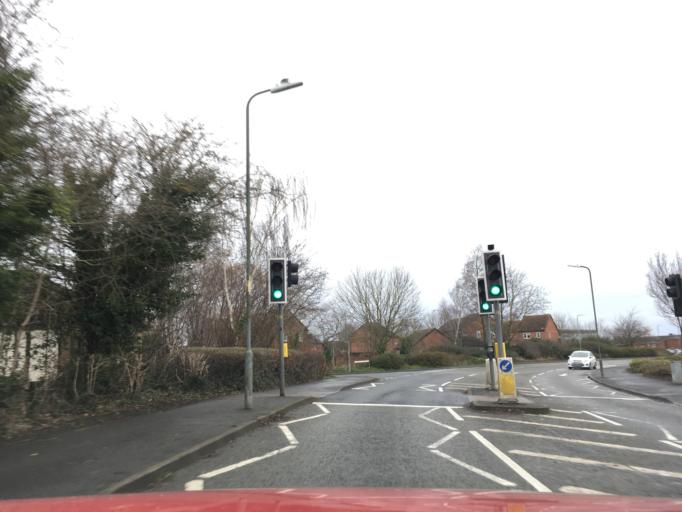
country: GB
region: England
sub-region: Worcestershire
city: Evesham
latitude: 52.0784
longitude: -1.9418
